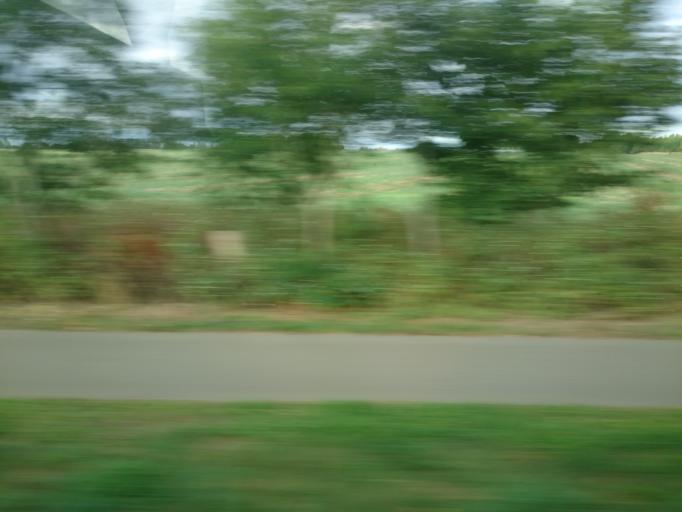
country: DE
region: Mecklenburg-Vorpommern
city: Pasewalk
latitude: 53.5330
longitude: 13.9739
